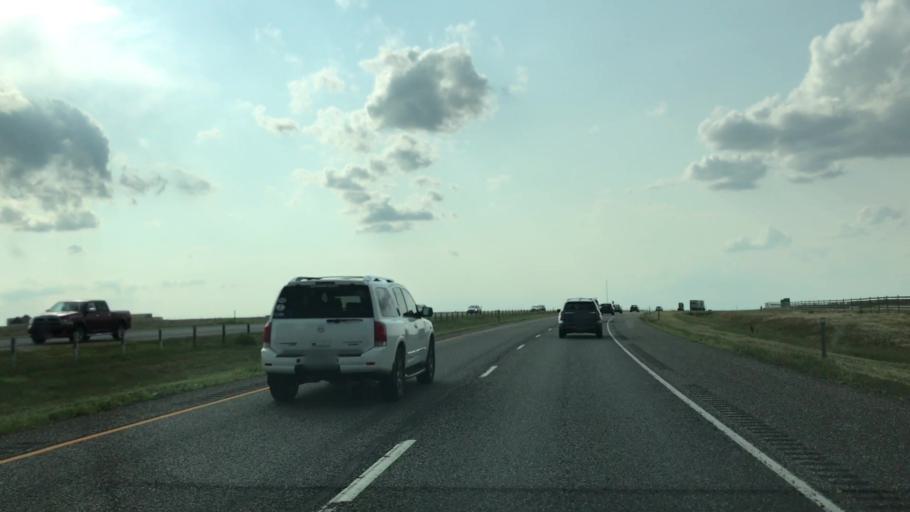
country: US
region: Colorado
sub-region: Adams County
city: Aurora
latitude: 39.8187
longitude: -104.7397
